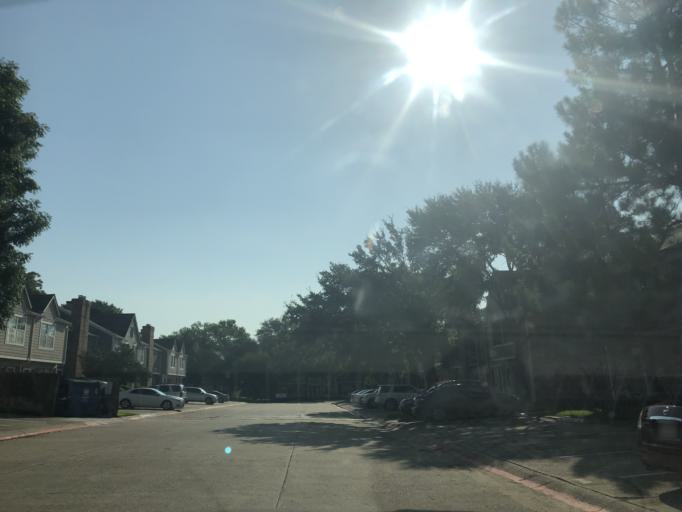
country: US
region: Texas
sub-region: Tarrant County
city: Euless
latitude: 32.8682
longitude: -97.0816
